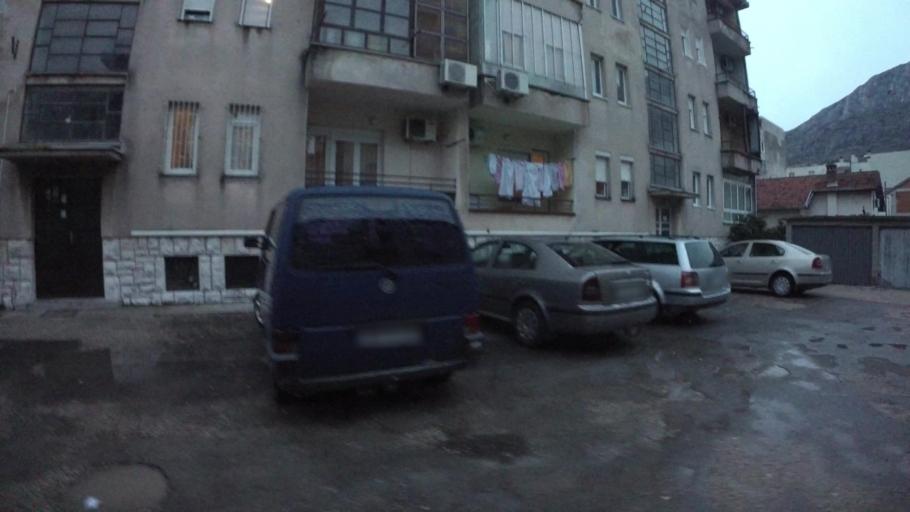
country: BA
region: Federation of Bosnia and Herzegovina
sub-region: Hercegovacko-Bosanski Kanton
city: Mostar
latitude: 43.3278
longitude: 17.8212
